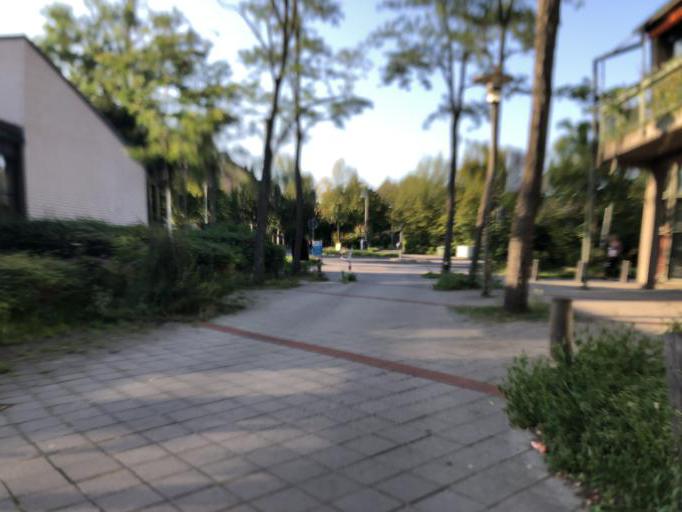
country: DE
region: Bavaria
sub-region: Regierungsbezirk Mittelfranken
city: Erlangen
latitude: 49.5955
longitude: 10.9618
